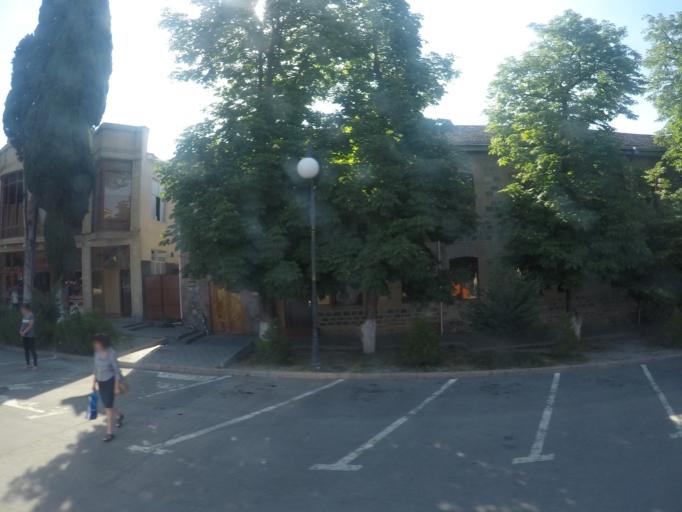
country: AZ
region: Shaki City
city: Sheki
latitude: 41.2035
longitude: 47.1788
